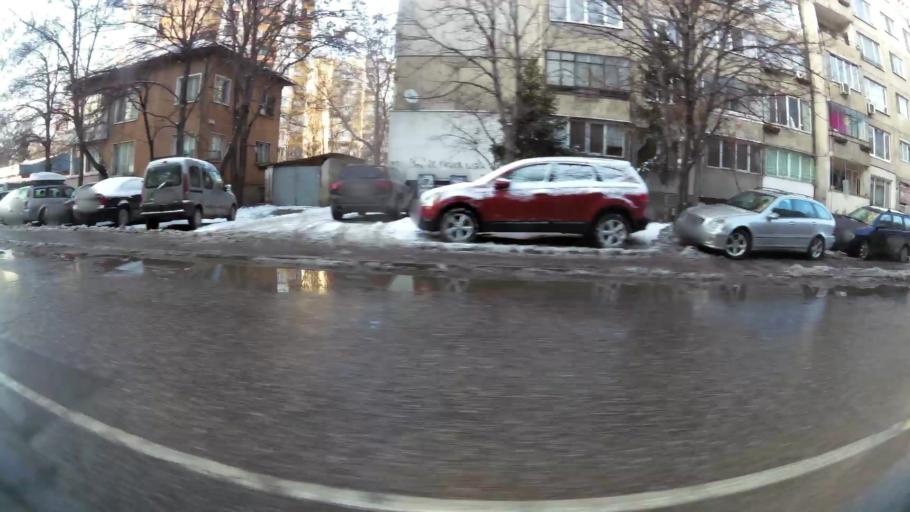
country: BG
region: Sofia-Capital
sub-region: Stolichna Obshtina
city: Sofia
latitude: 42.6802
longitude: 23.3760
